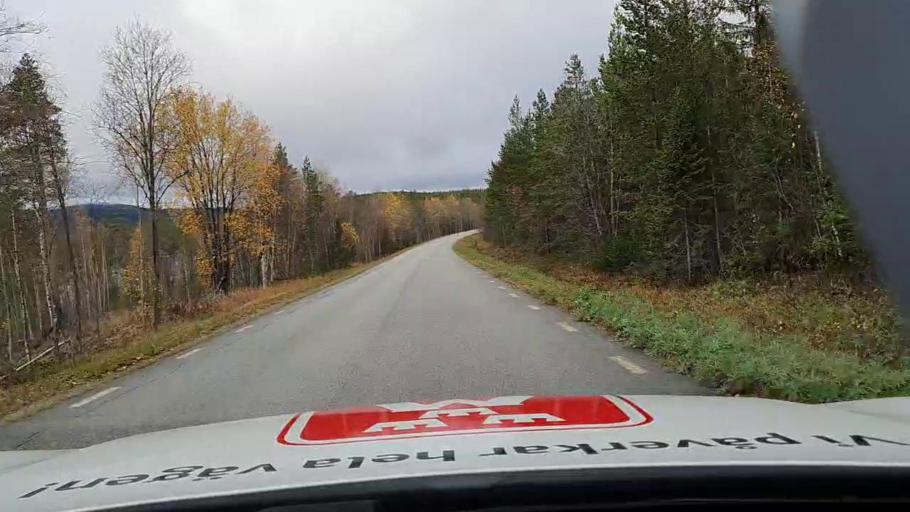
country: SE
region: Jaemtland
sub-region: Bergs Kommun
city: Hoverberg
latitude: 63.0339
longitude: 14.0445
